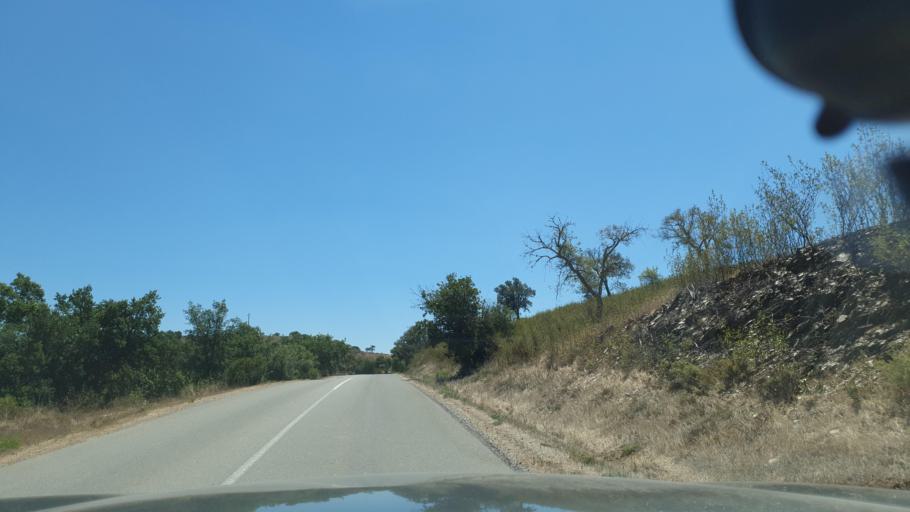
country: PT
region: Beja
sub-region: Ourique
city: Ourique
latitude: 37.5517
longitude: -8.4192
